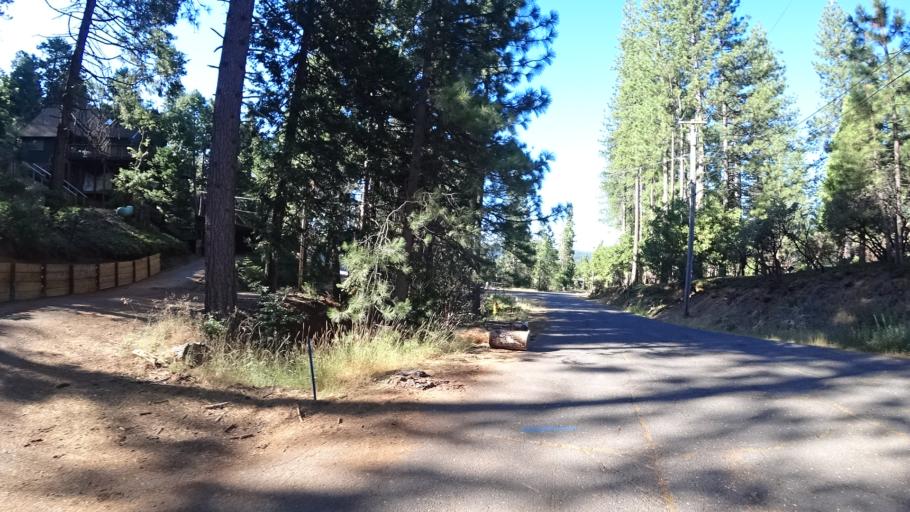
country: US
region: California
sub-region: Calaveras County
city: Arnold
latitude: 38.2639
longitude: -120.3266
